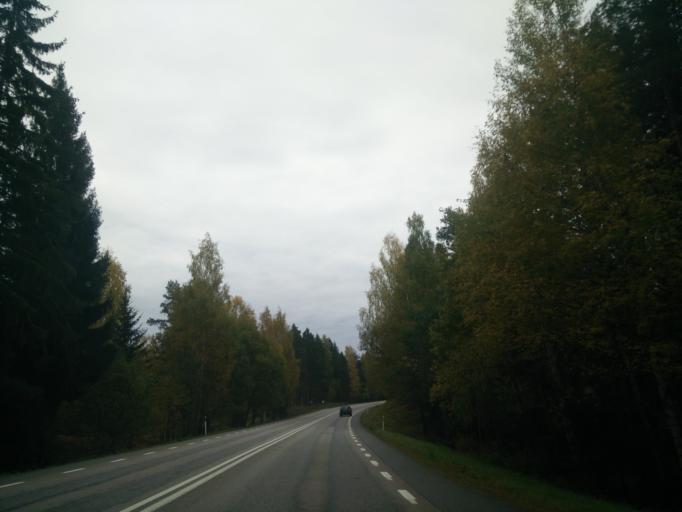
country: SE
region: Gaevleborg
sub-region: Gavle Kommun
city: Norrsundet
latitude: 60.8890
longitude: 17.1228
